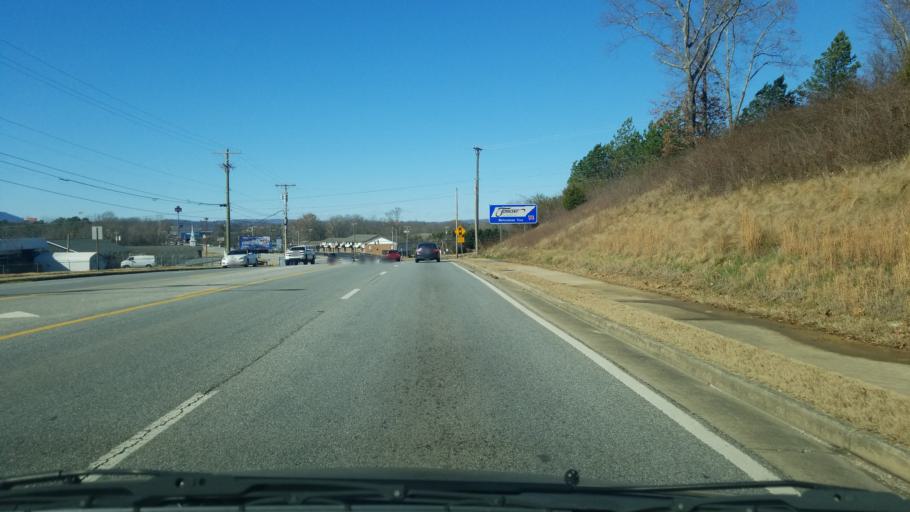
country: US
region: Georgia
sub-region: Catoosa County
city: Indian Springs
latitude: 34.9873
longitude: -85.1896
